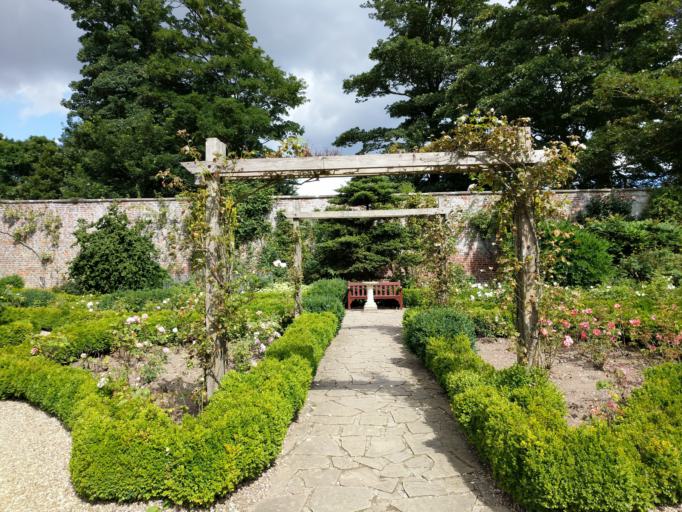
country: GB
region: England
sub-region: East Riding of Yorkshire
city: Bempton
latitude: 54.1044
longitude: -0.1578
